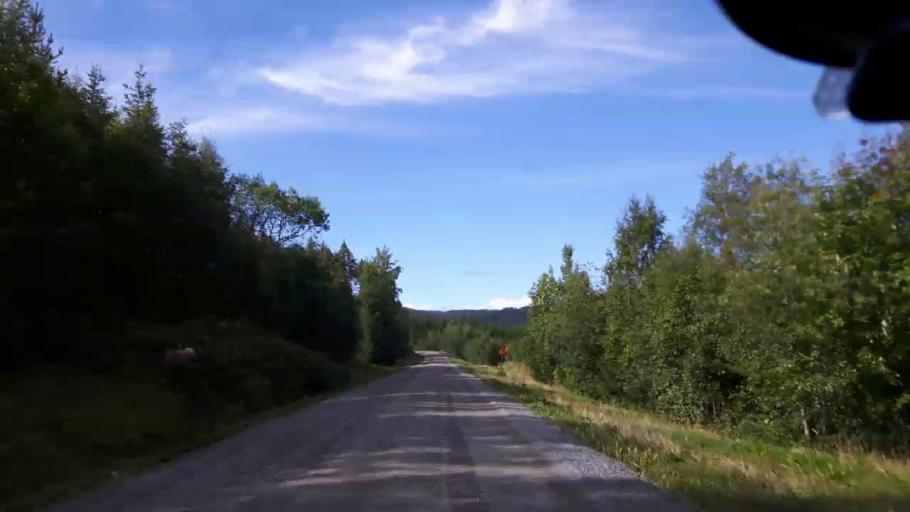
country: SE
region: Jaemtland
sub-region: Ragunda Kommun
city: Hammarstrand
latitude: 63.1347
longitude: 16.1123
